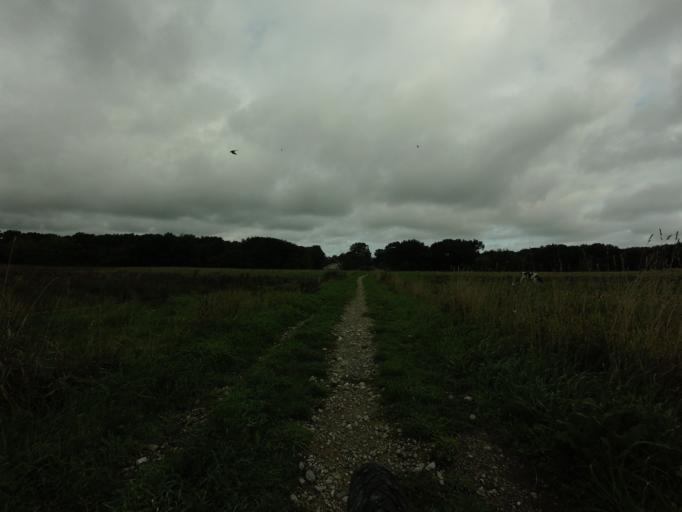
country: DK
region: North Denmark
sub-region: Hjorring Kommune
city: Hjorring
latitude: 57.4780
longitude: 9.9775
